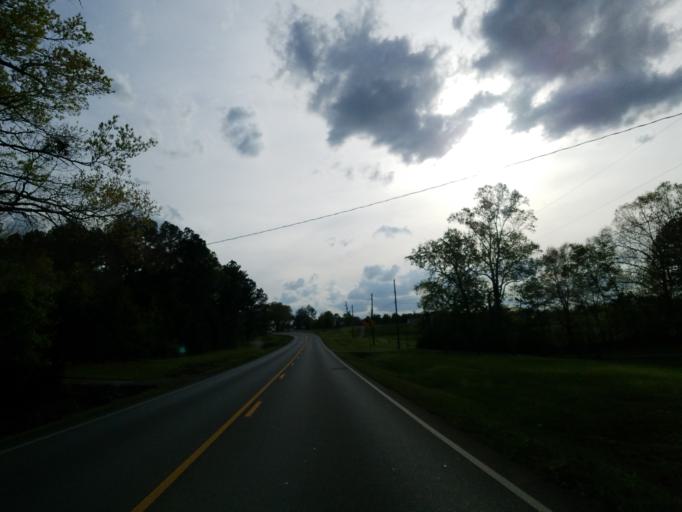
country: US
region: Georgia
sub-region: Cherokee County
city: Ball Ground
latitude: 34.2602
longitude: -84.3208
